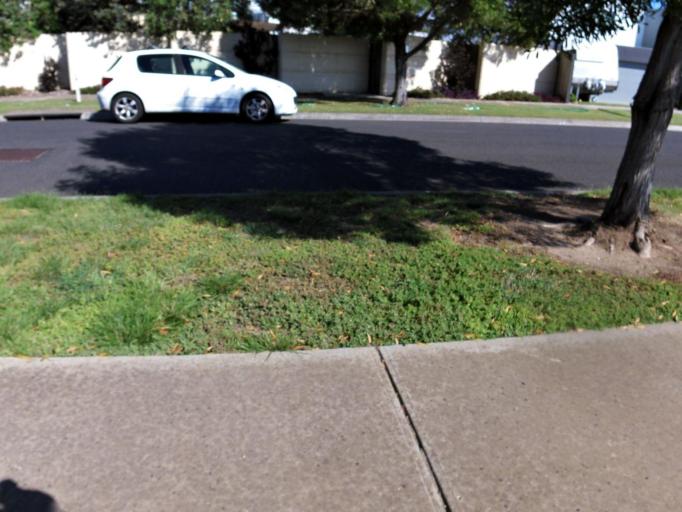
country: AU
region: Victoria
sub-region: Greater Geelong
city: Wandana Heights
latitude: -38.1515
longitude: 144.3041
